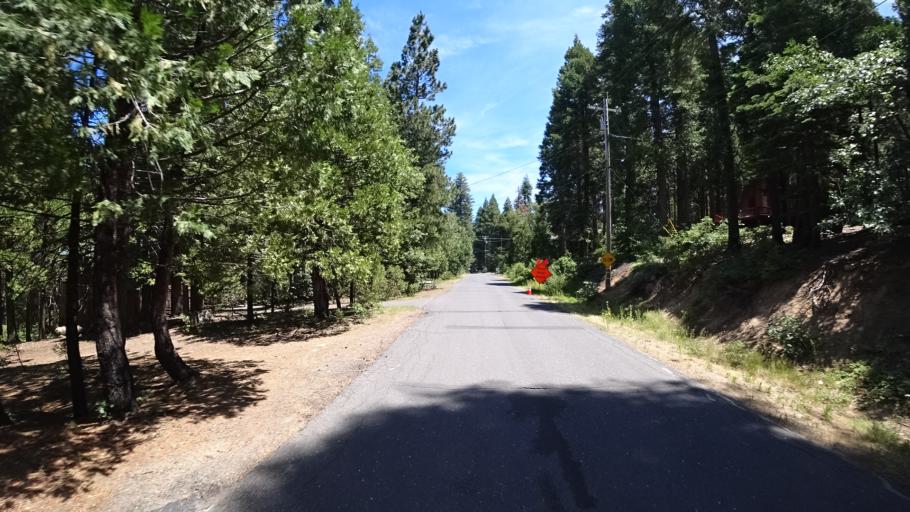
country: US
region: California
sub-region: Calaveras County
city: Arnold
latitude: 38.3162
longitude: -120.2607
